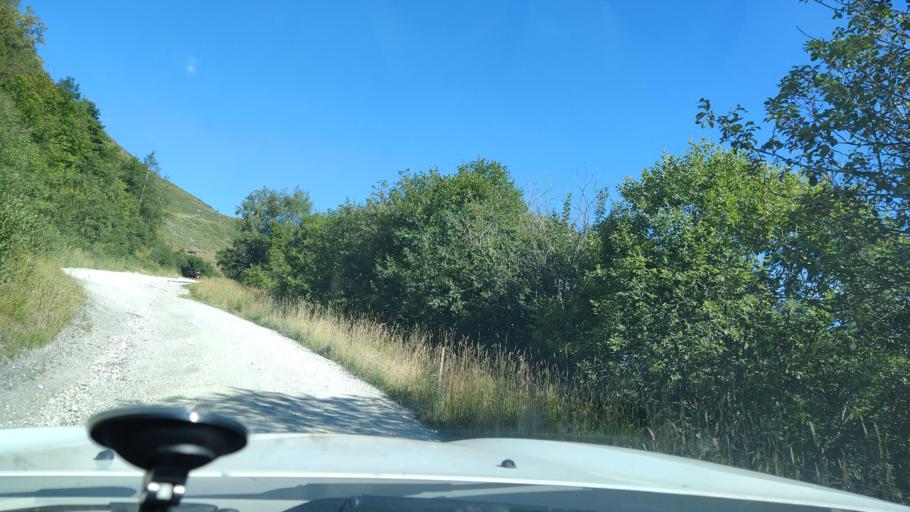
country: FR
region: Rhone-Alpes
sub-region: Departement de la Savoie
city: Val Thorens
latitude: 45.3208
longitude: 6.5326
